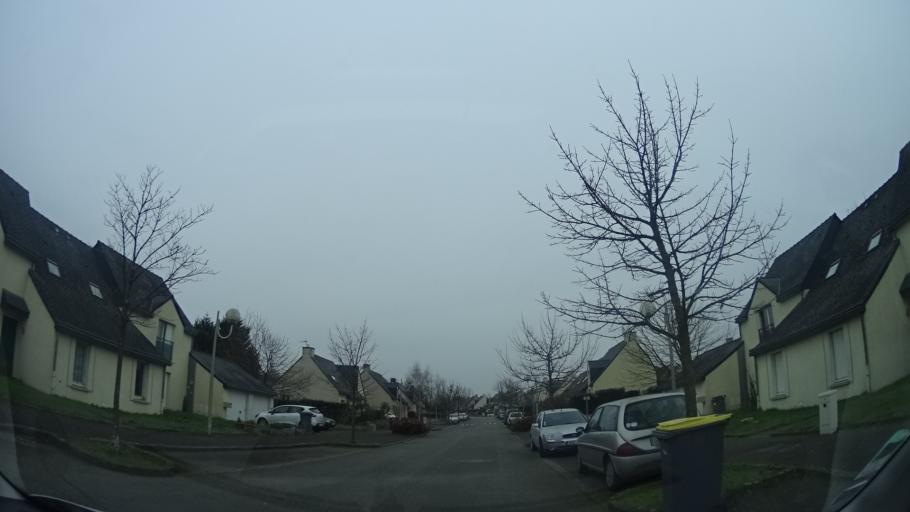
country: FR
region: Brittany
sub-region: Departement d'Ille-et-Vilaine
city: Brece
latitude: 48.1061
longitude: -1.4788
